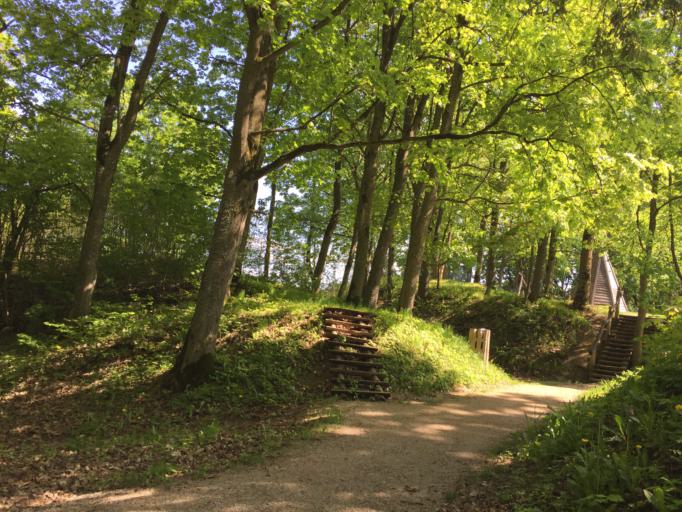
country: LV
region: Rundales
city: Pilsrundale
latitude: 56.4409
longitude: 24.0451
